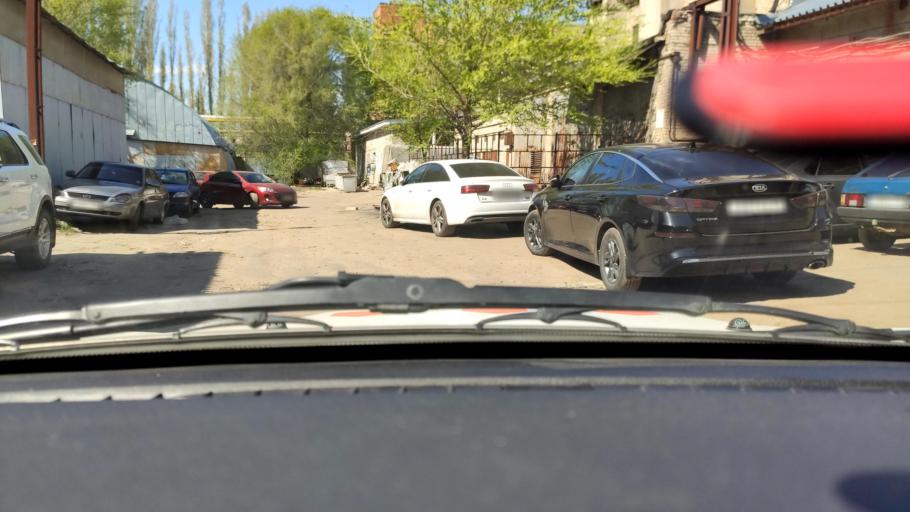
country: RU
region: Voronezj
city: Voronezh
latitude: 51.6821
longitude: 39.1789
